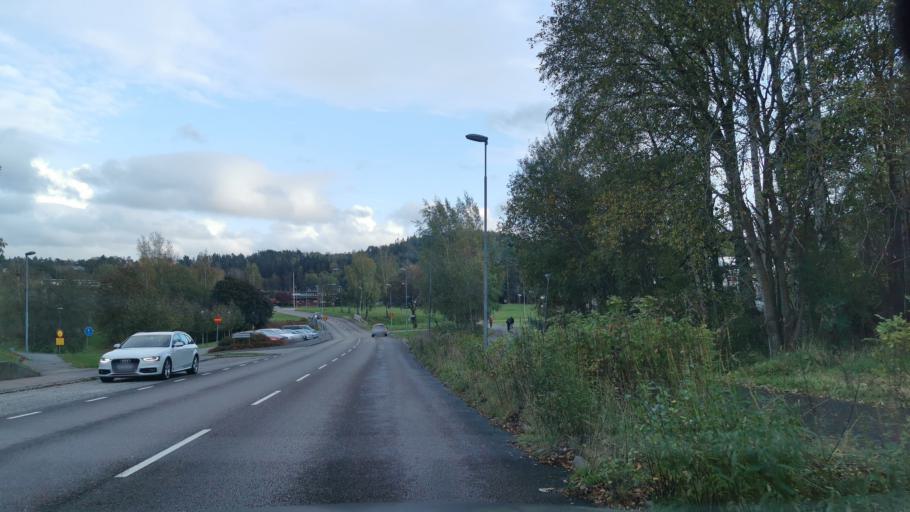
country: SE
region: Vaestra Goetaland
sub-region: Partille Kommun
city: Partille
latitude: 57.7170
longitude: 12.0718
